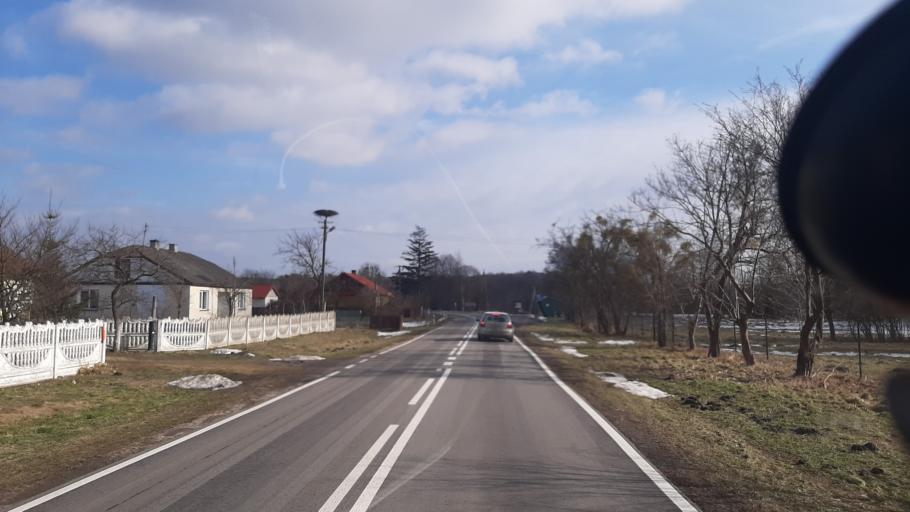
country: PL
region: Lublin Voivodeship
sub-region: Powiat parczewski
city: Sosnowica
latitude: 51.4965
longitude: 23.1717
